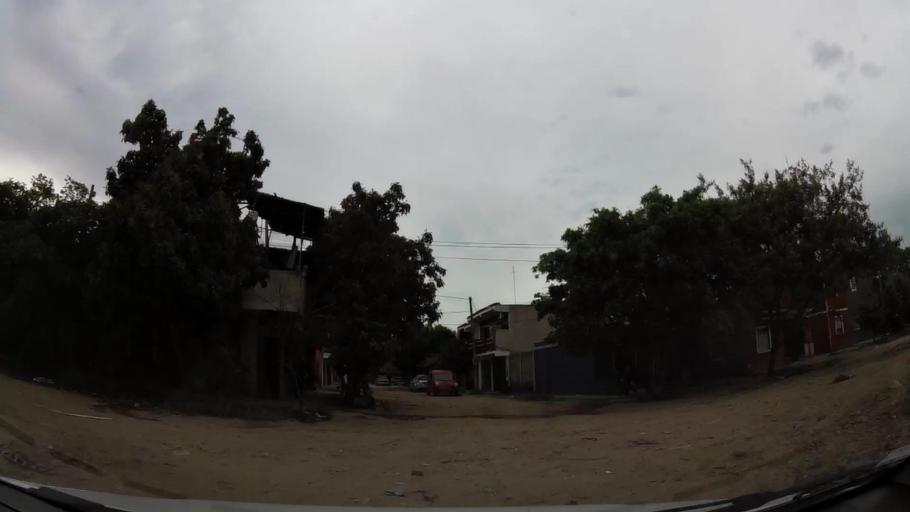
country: AR
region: Buenos Aires
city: San Justo
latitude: -34.6764
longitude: -58.5233
